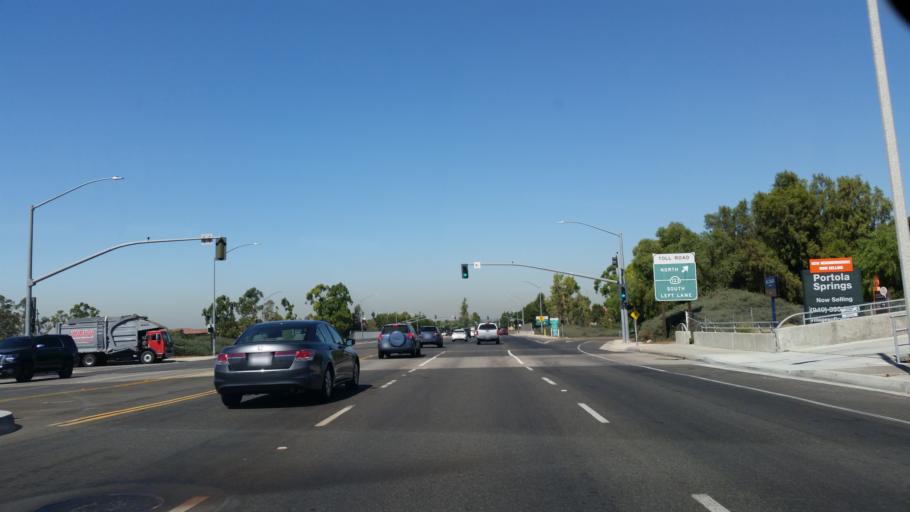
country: US
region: California
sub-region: Orange County
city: Lake Forest
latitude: 33.6957
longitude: -117.7340
